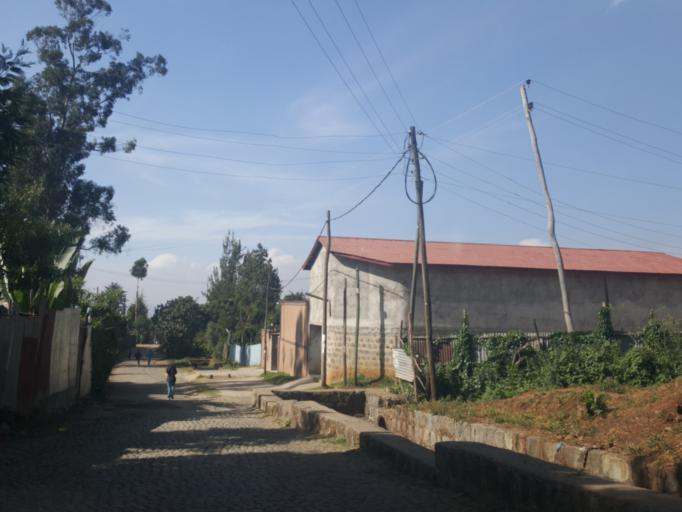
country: ET
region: Adis Abeba
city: Addis Ababa
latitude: 9.0543
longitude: 38.7285
